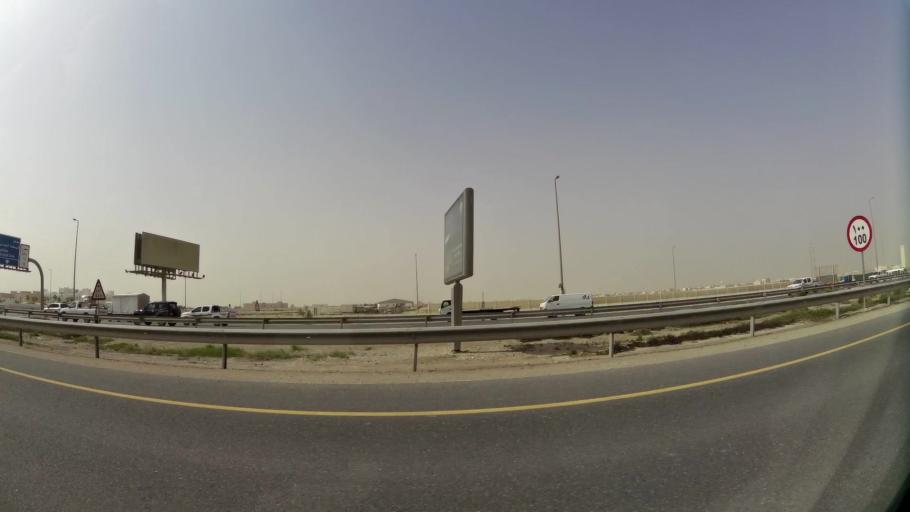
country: QA
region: Baladiyat ar Rayyan
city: Ar Rayyan
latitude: 25.2154
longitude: 51.4145
